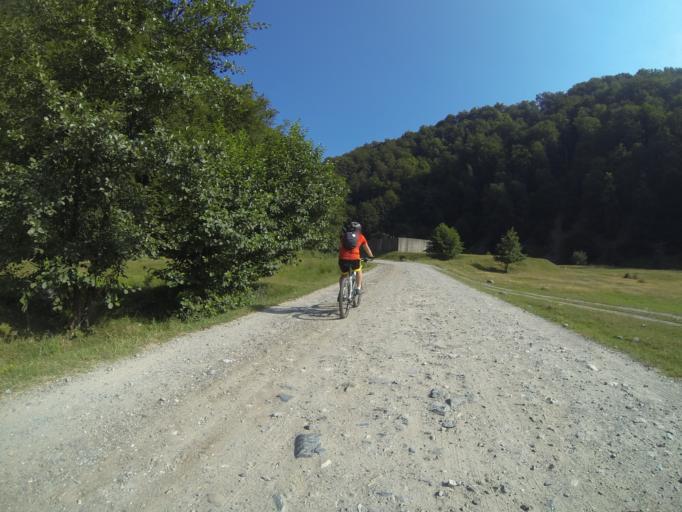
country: RO
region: Valcea
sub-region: Comuna Costesti
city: Bistrita
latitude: 45.2046
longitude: 23.9992
